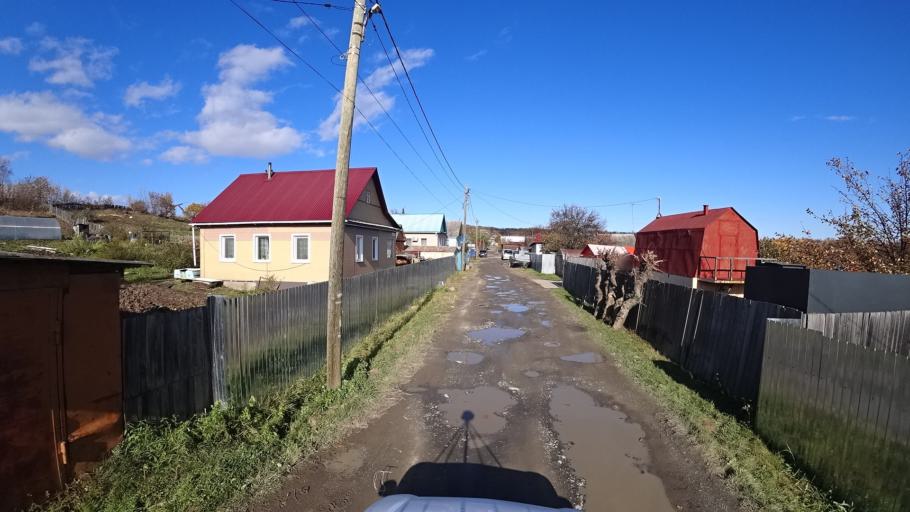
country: RU
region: Khabarovsk Krai
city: Amursk
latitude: 50.2319
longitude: 136.9191
